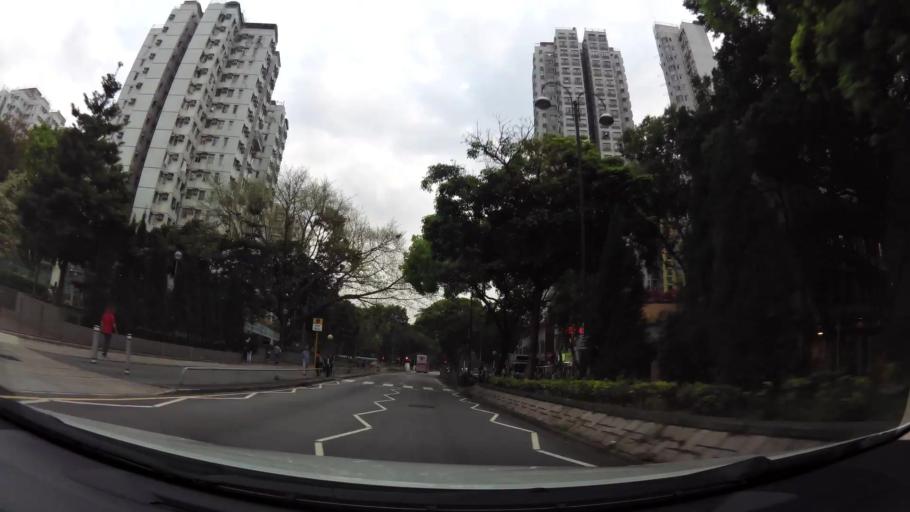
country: HK
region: Tai Po
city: Tai Po
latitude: 22.4541
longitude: 114.1661
